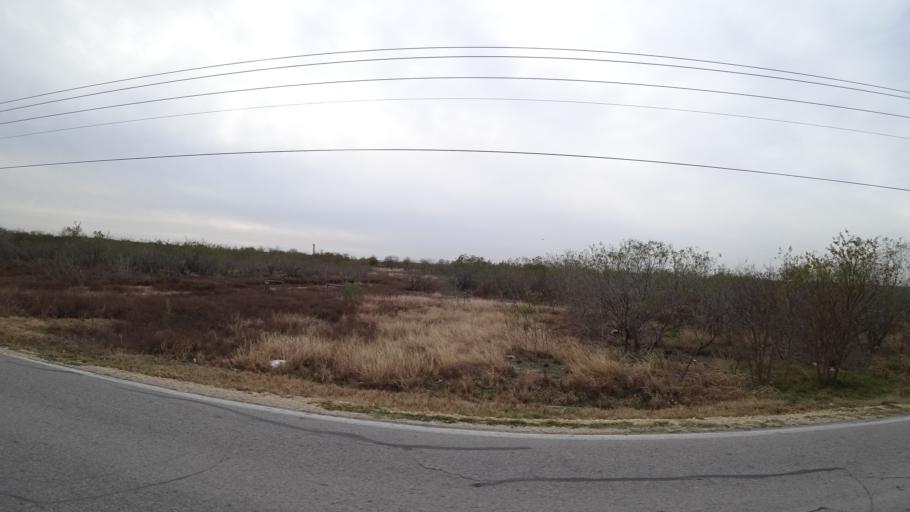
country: US
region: Texas
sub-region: Travis County
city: Garfield
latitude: 30.1524
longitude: -97.6365
